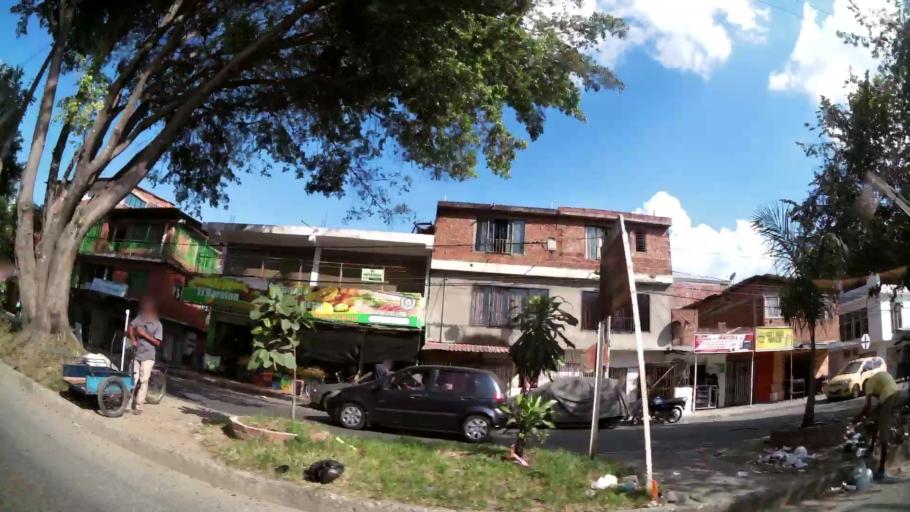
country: CO
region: Valle del Cauca
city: Cali
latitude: 3.4195
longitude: -76.4937
